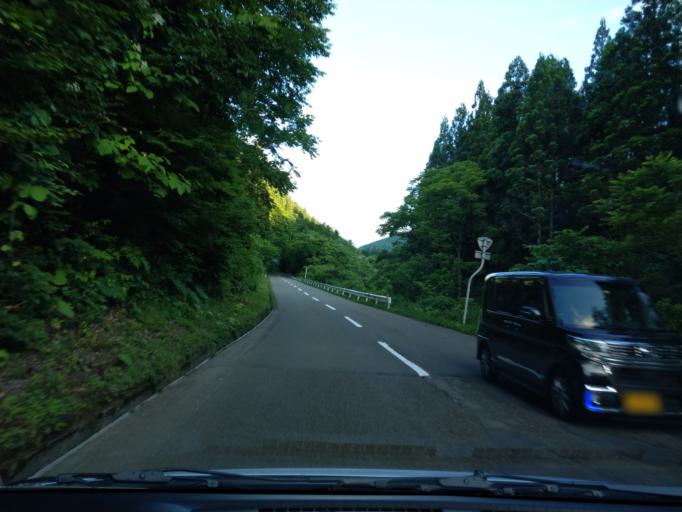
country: JP
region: Akita
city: Kakunodatemachi
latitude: 39.8900
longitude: 140.4656
